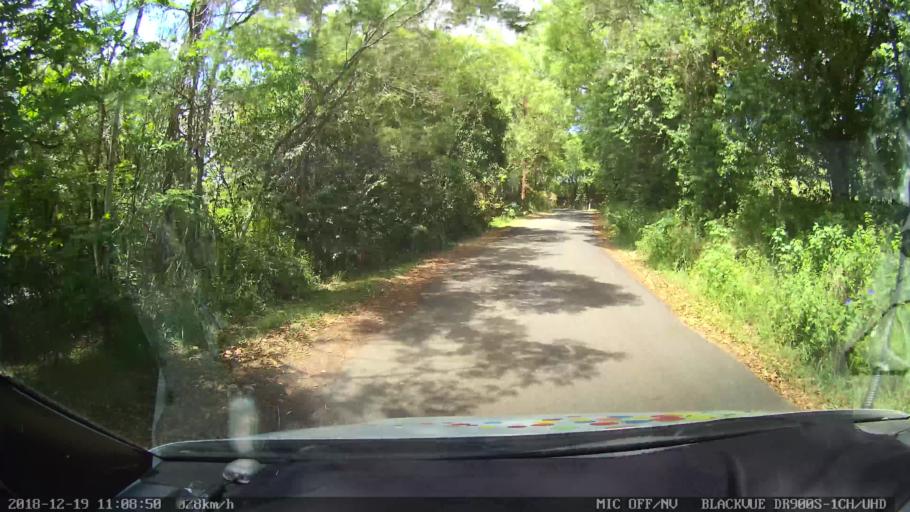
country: AU
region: New South Wales
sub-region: Lismore Municipality
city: Nimbin
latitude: -28.6316
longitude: 153.2646
